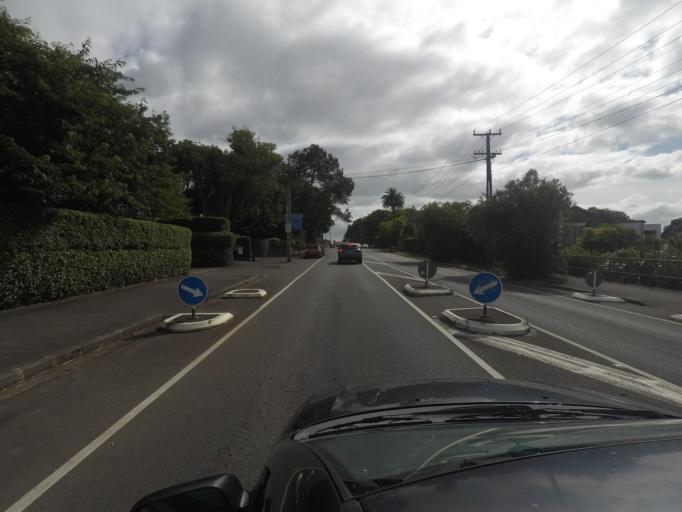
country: NZ
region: Auckland
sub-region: Auckland
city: Auckland
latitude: -36.8802
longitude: 174.7887
